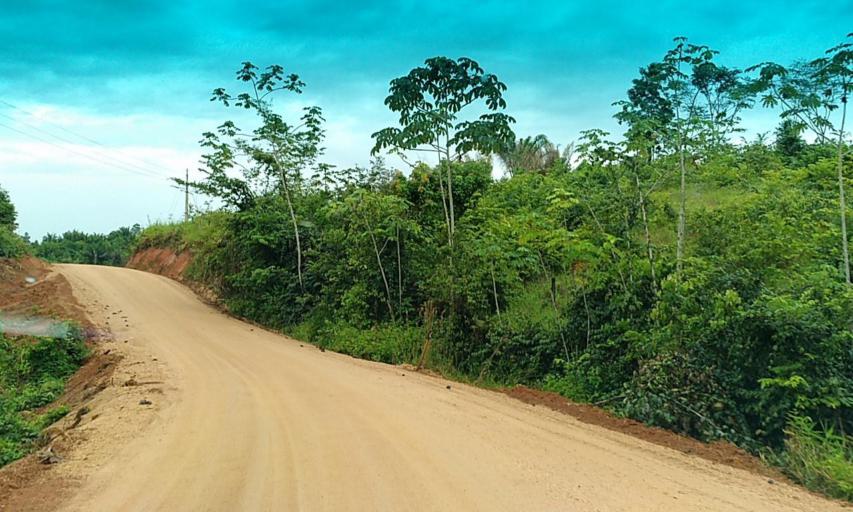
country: BR
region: Para
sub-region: Senador Jose Porfirio
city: Senador Jose Porfirio
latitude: -3.0794
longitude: -51.6341
